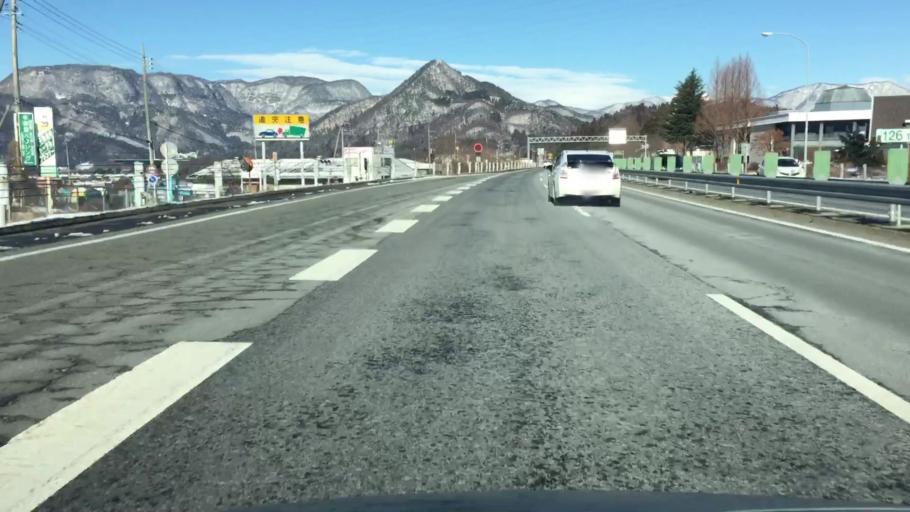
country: JP
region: Gunma
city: Numata
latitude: 36.6588
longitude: 139.0687
